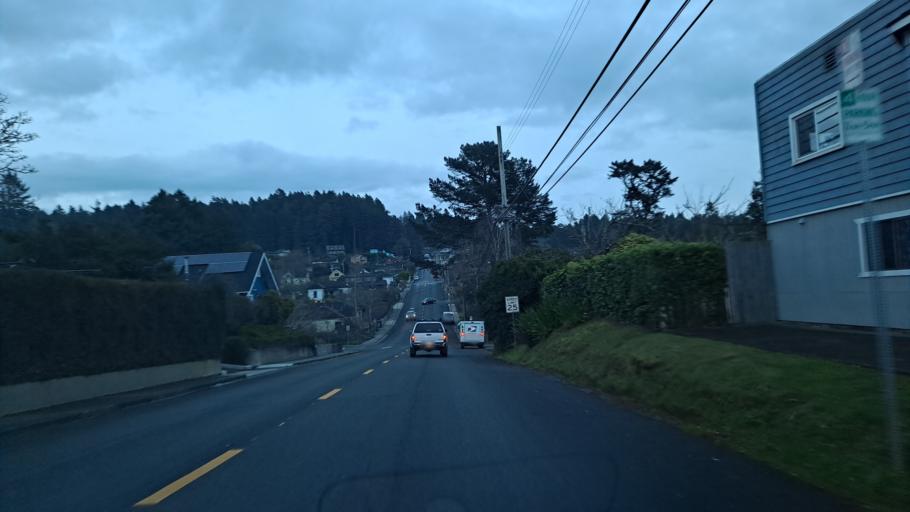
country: US
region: California
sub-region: Humboldt County
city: Arcata
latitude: 40.8695
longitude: -124.0809
